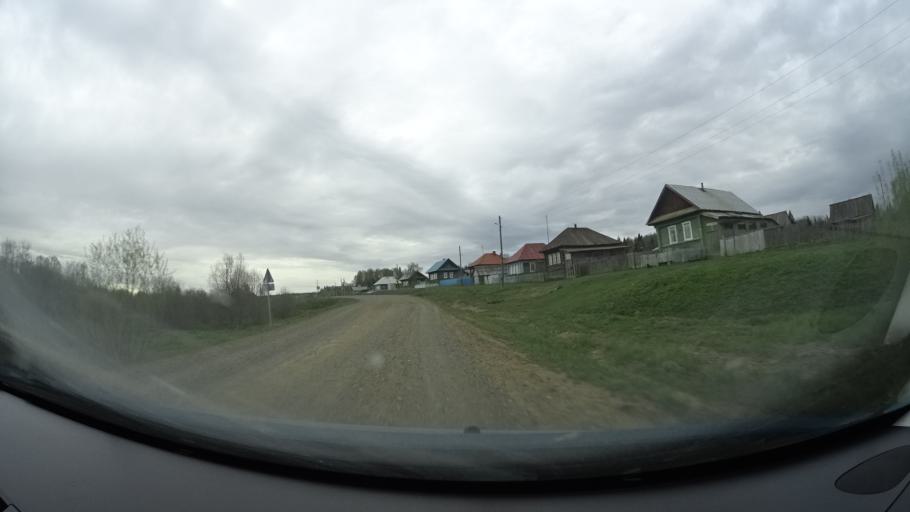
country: RU
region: Perm
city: Kuyeda
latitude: 56.6154
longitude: 55.7094
